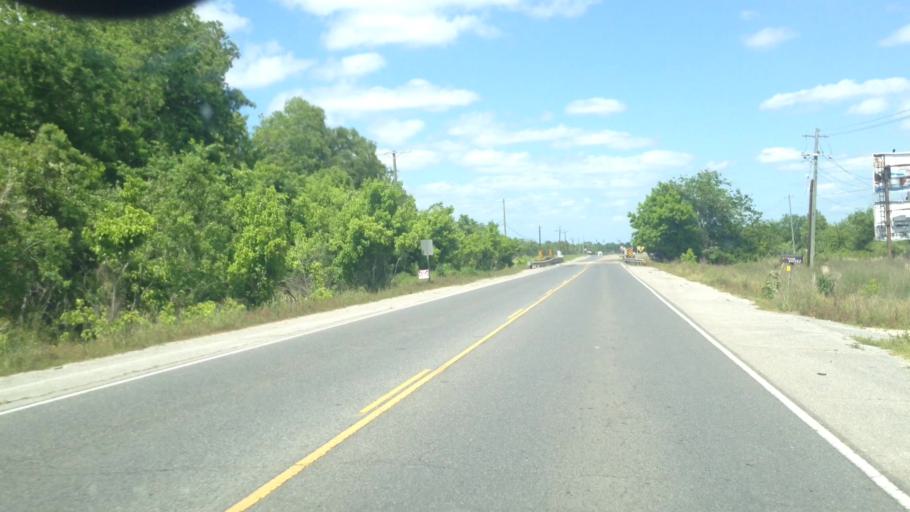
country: US
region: Louisiana
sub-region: Terrebonne Parish
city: Houma
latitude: 29.6522
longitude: -90.6817
